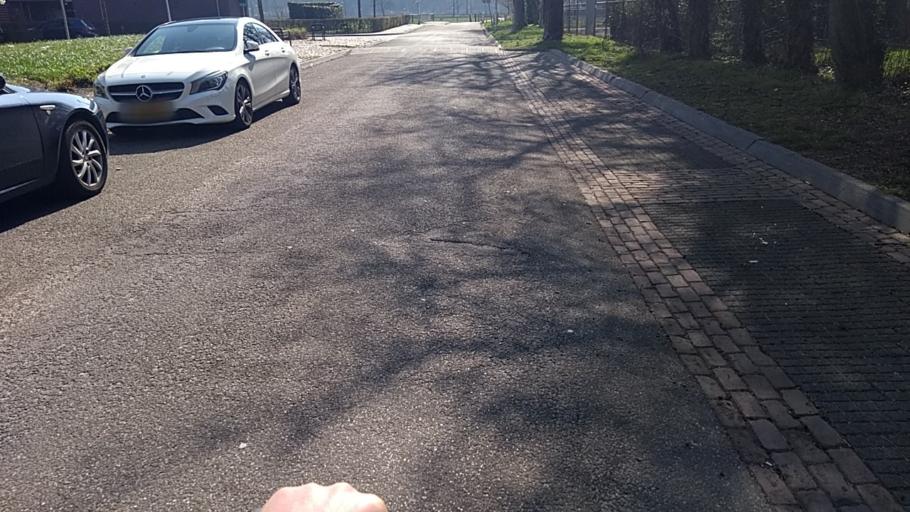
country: NL
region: Overijssel
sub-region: Gemeente Almelo
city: Almelo
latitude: 52.3419
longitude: 6.6727
